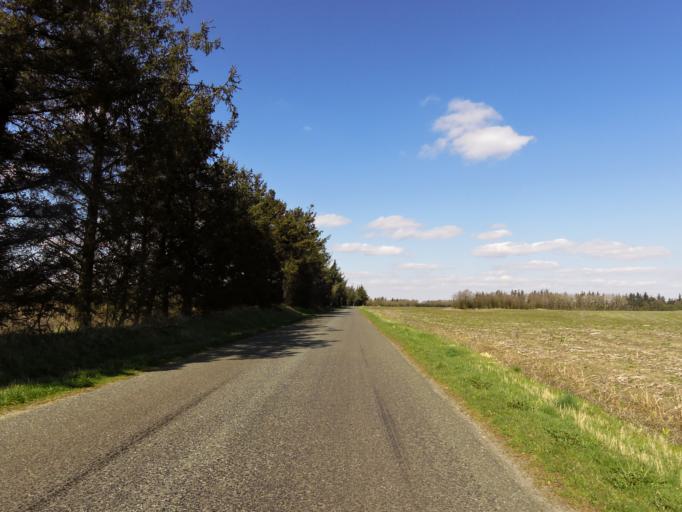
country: DK
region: South Denmark
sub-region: Esbjerg Kommune
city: Ribe
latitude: 55.3371
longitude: 8.8326
